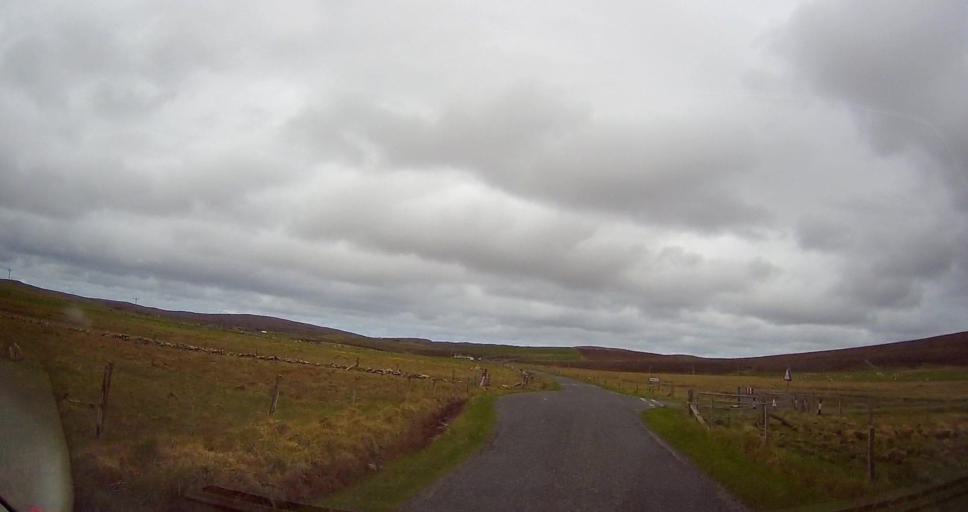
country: GB
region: Scotland
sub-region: Shetland Islands
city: Shetland
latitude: 60.7917
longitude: -0.8471
